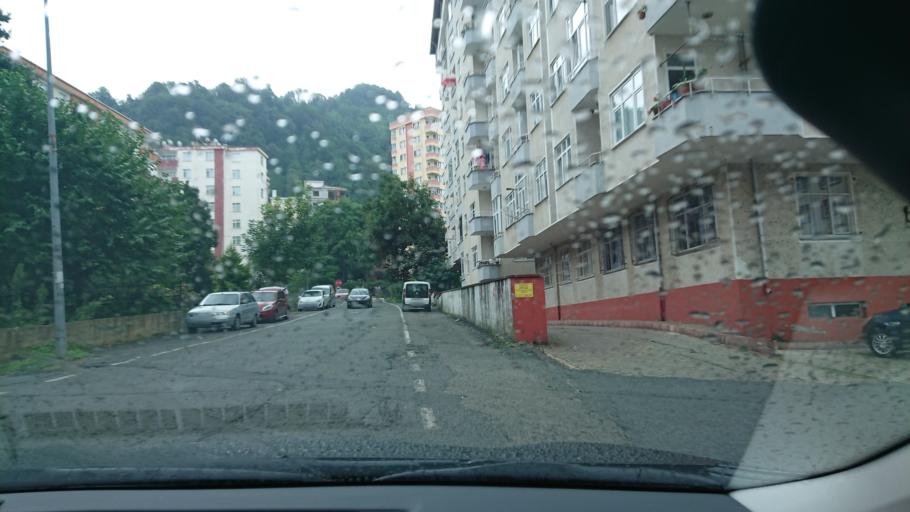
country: TR
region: Rize
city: Rize
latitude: 41.0259
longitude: 40.5465
